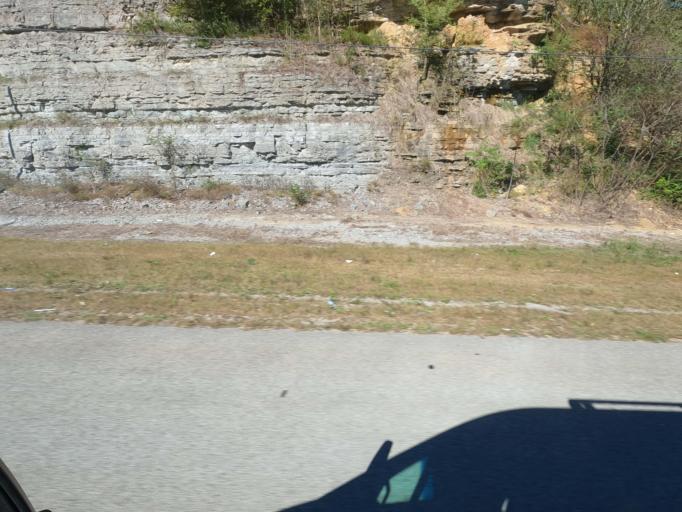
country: US
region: Tennessee
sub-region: Maury County
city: Mount Pleasant
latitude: 35.4838
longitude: -87.2526
